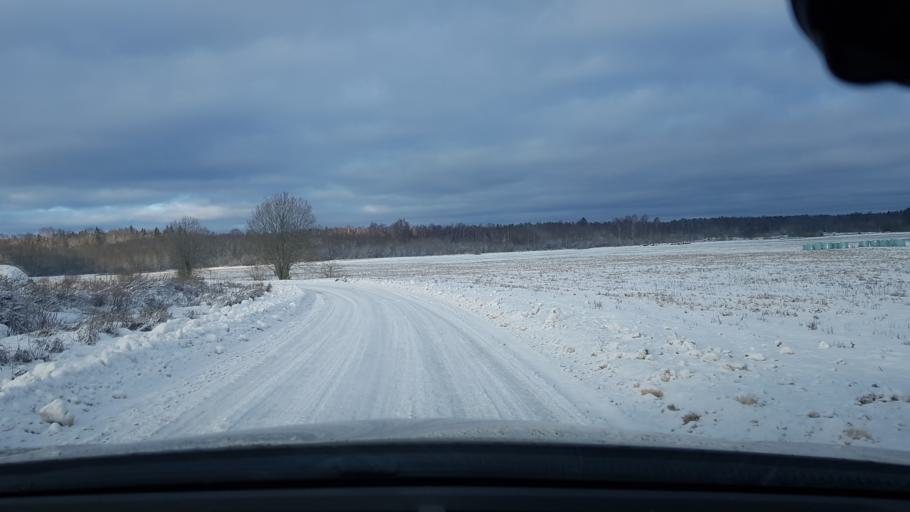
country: EE
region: Harju
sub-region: Keila linn
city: Keila
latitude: 59.3124
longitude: 24.2525
